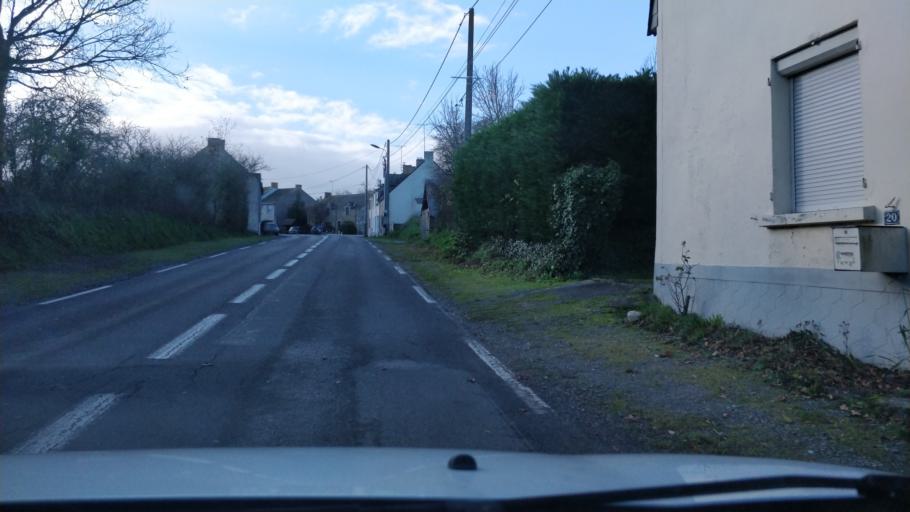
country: FR
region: Pays de la Loire
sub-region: Departement de la Loire-Atlantique
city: Asserac
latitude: 47.4168
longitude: -2.4001
